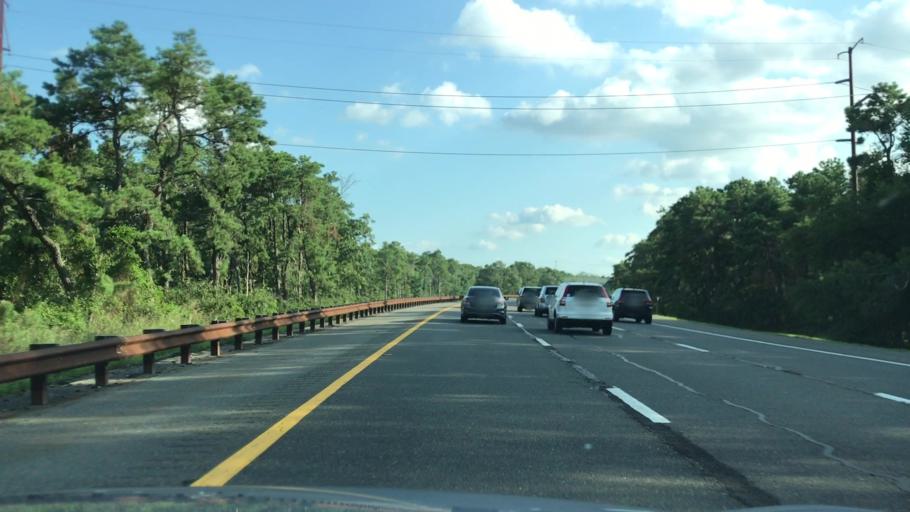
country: US
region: New Jersey
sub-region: Ocean County
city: Waretown
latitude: 39.8000
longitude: -74.2350
